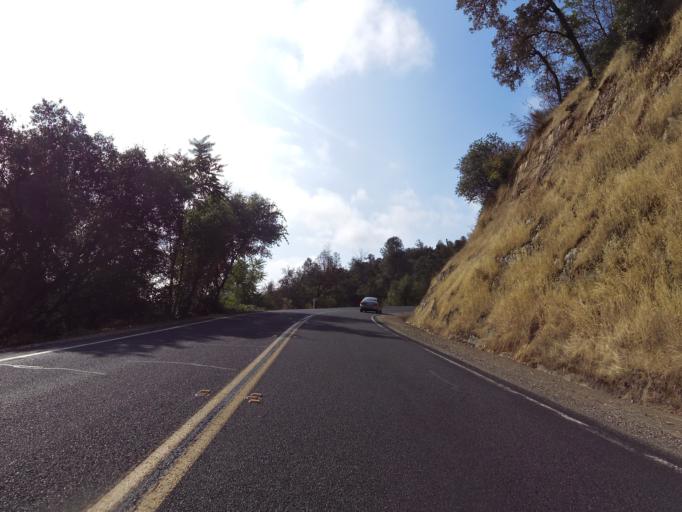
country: US
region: California
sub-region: Tuolumne County
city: Jamestown
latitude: 37.9912
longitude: -120.4690
